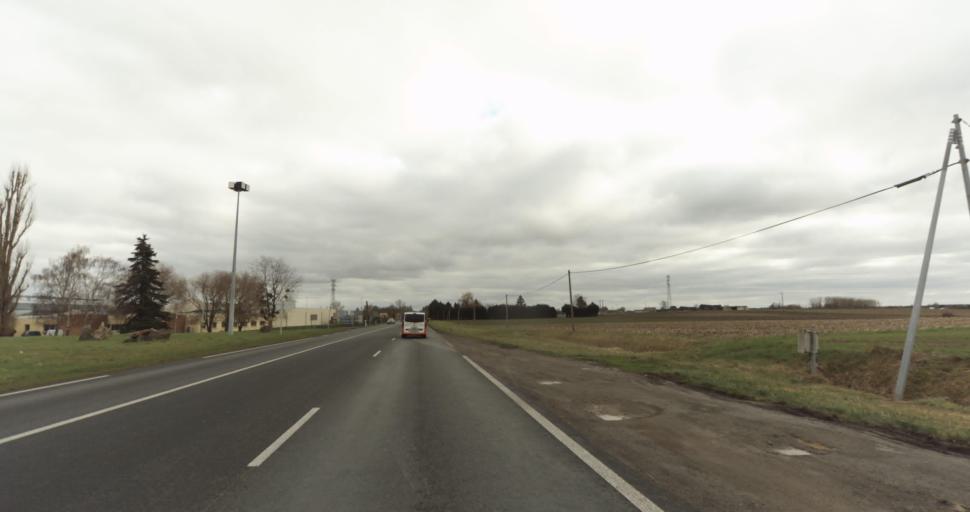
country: FR
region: Pays de la Loire
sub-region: Departement de Maine-et-Loire
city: Saint-Philbert-du-Peuple
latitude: 47.3687
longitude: -0.0970
